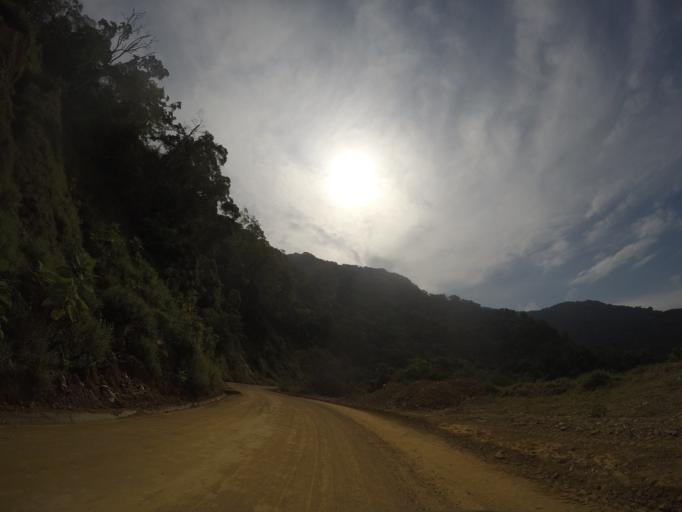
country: MX
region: Oaxaca
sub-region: San Pedro Pochutla
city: Los Naranjos Esquipulas
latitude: 15.9531
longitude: -96.4480
